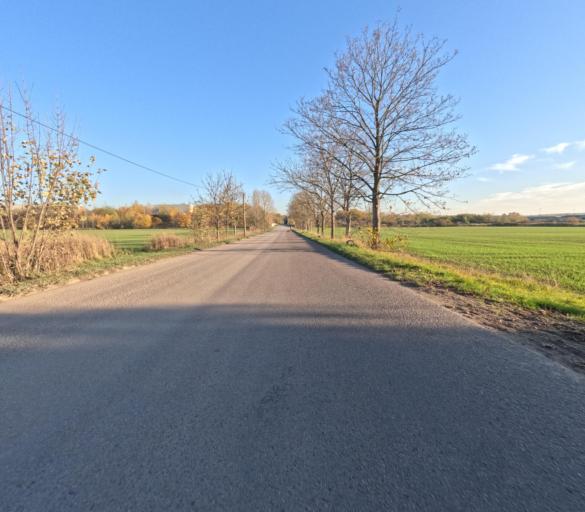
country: DE
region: Saxony
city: Otterwisch
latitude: 51.2514
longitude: 12.6469
